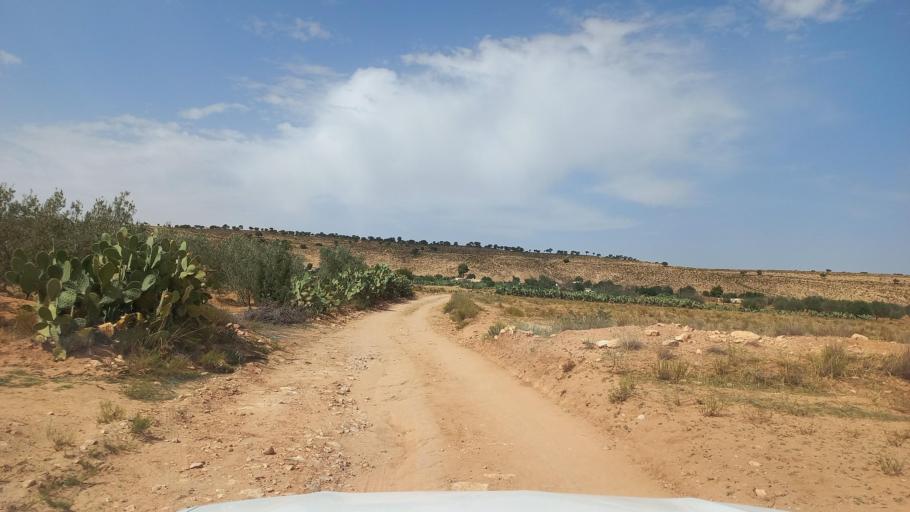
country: TN
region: Al Qasrayn
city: Kasserine
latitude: 35.3676
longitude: 8.8808
